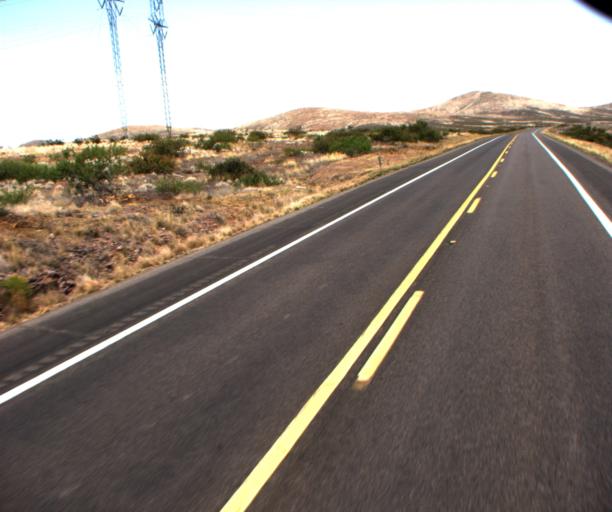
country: US
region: Arizona
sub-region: Greenlee County
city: Clifton
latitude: 32.7454
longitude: -109.2205
